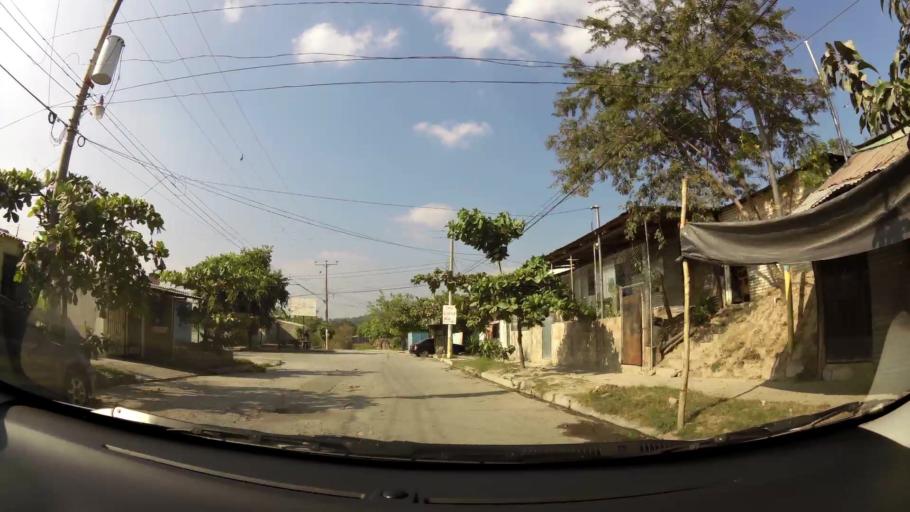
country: SV
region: San Salvador
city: Ilopango
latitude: 13.7293
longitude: -89.1101
